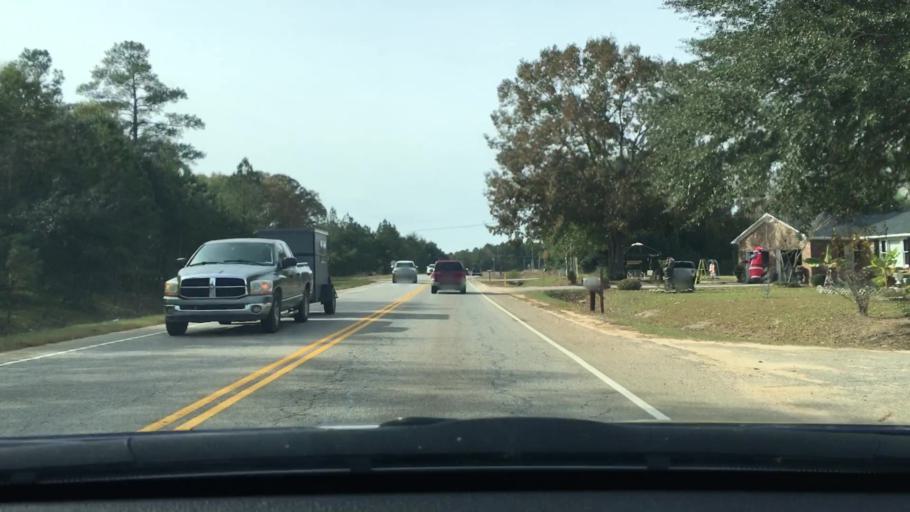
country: US
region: South Carolina
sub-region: Sumter County
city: Cherryvale
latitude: 33.9377
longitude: -80.4701
